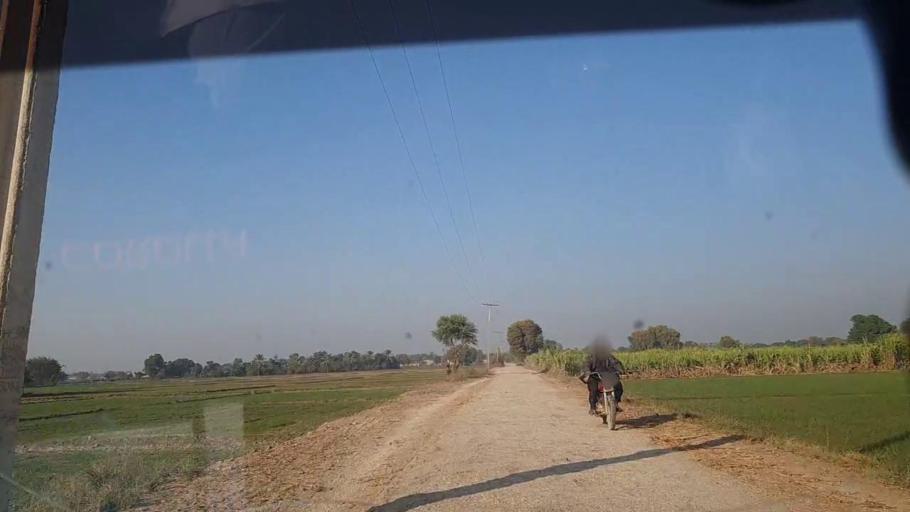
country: PK
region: Sindh
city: Sobhadero
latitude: 27.2491
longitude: 68.3499
